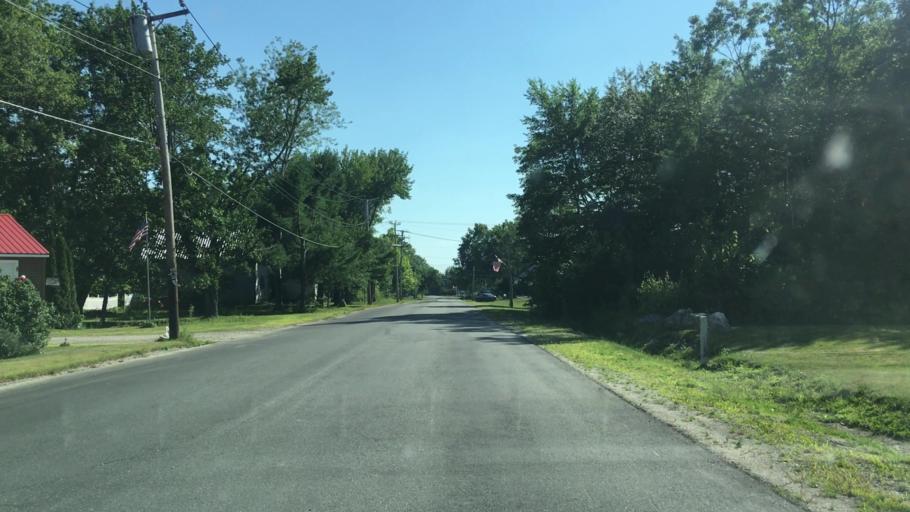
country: US
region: Maine
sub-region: Penobscot County
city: Howland
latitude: 45.2428
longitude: -68.6467
